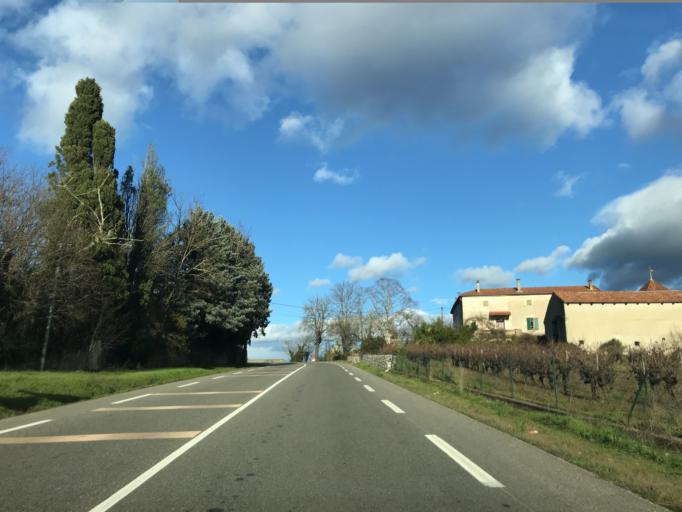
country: FR
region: Rhone-Alpes
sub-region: Departement de l'Ardeche
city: Largentiere
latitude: 44.5087
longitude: 4.3163
